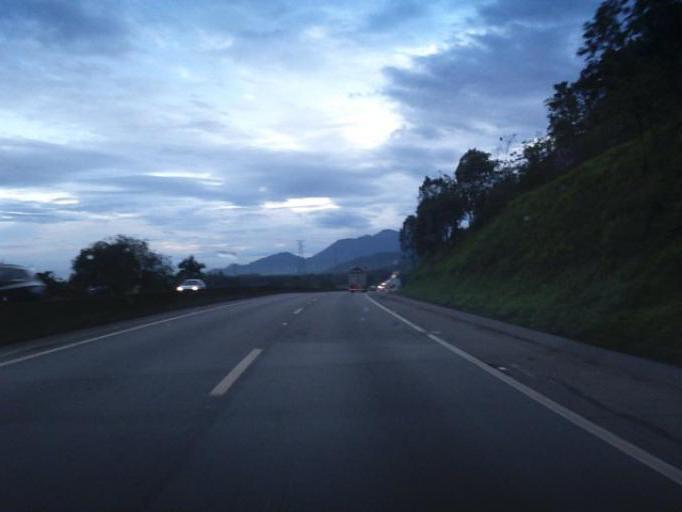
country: BR
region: Santa Catarina
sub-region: Joinville
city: Joinville
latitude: -26.1138
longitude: -48.8761
